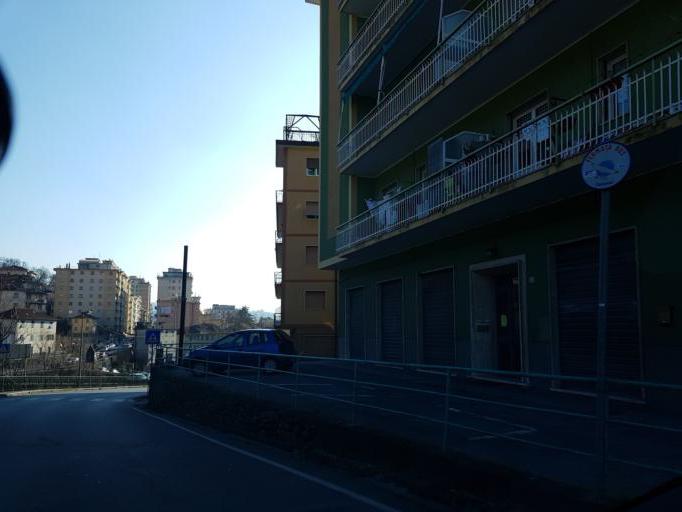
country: IT
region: Liguria
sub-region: Provincia di Genova
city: Campomorone
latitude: 44.5109
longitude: 8.8822
